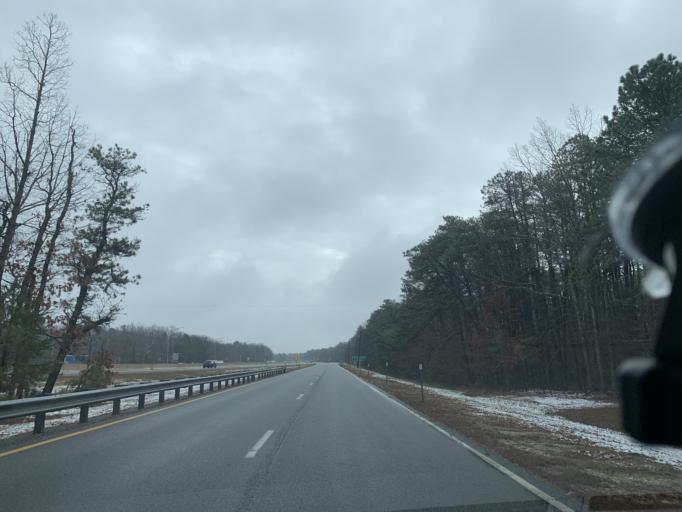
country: US
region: New Jersey
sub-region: Atlantic County
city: Pomona
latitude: 39.4479
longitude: -74.6229
